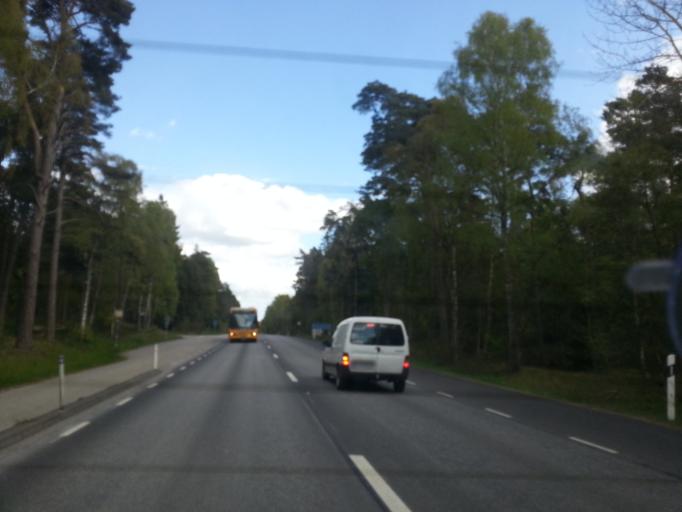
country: SE
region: Skane
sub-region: Ystads Kommun
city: Kopingebro
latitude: 55.4365
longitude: 13.9020
